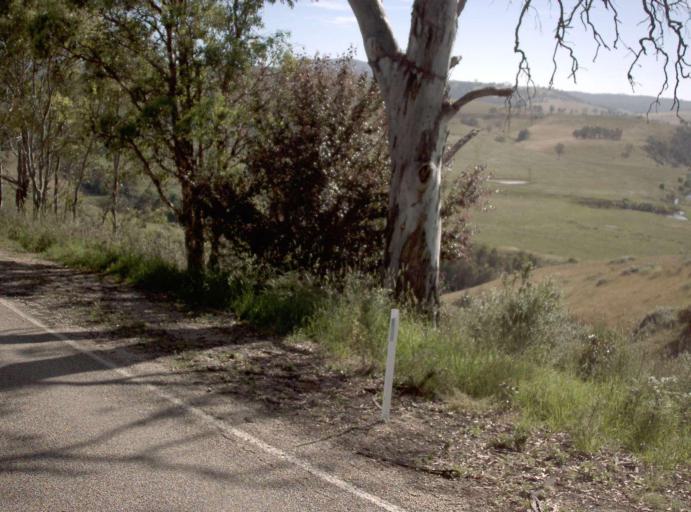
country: AU
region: Victoria
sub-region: East Gippsland
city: Lakes Entrance
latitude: -37.5090
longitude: 148.1706
